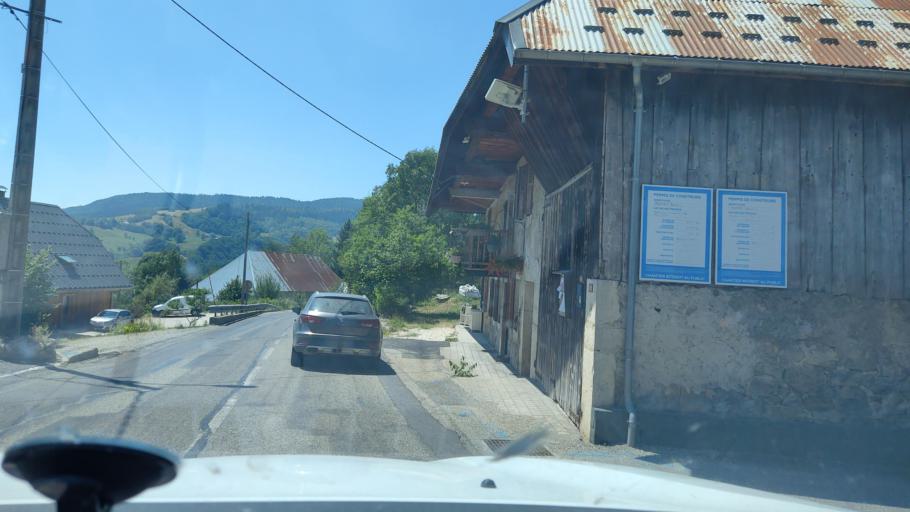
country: FR
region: Rhone-Alpes
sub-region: Departement de la Savoie
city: Barby
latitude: 45.6313
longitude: 6.0075
